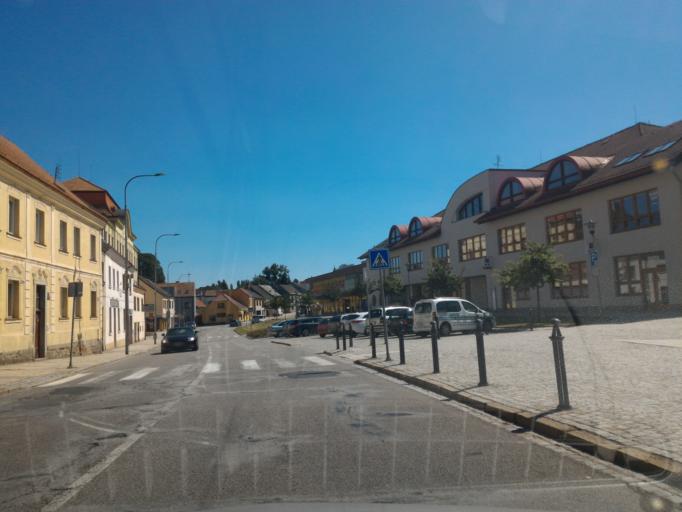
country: CZ
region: Vysocina
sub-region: Okres Jihlava
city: Trest'
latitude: 49.2911
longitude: 15.4832
